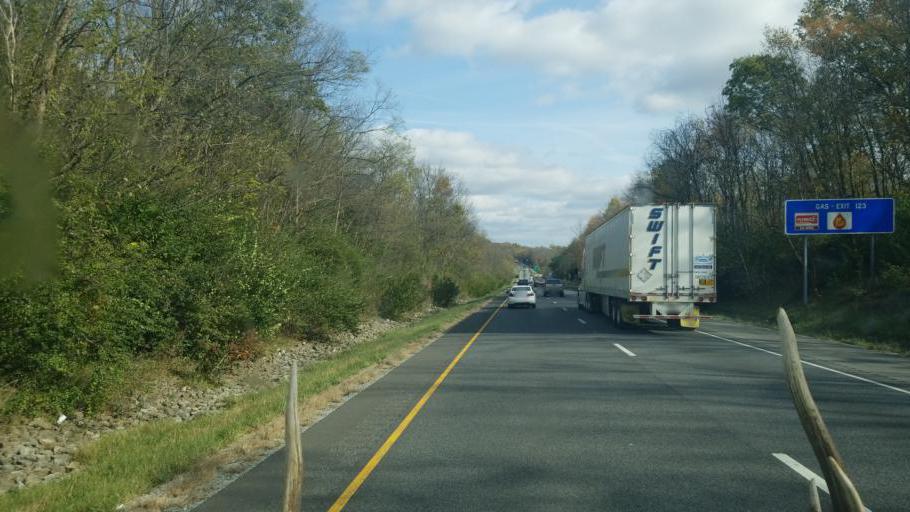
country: US
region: Indiana
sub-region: Henry County
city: Knightstown
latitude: 39.8533
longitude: -85.4488
